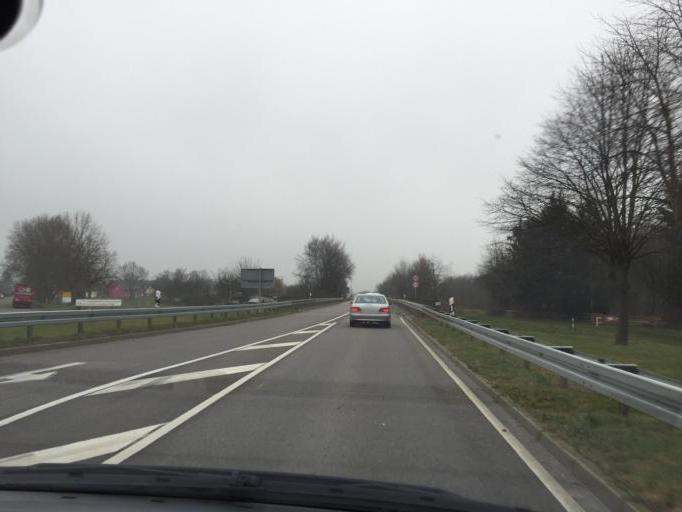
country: DE
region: Baden-Wuerttemberg
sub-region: Freiburg Region
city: Hartheim
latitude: 47.9606
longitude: 7.6624
